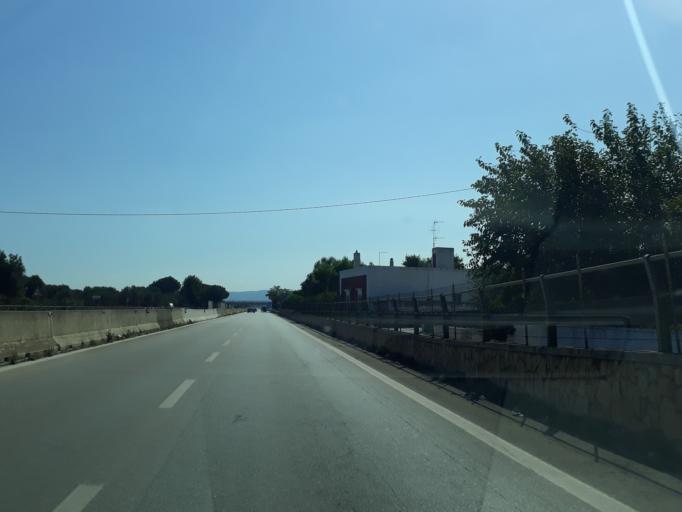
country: IT
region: Apulia
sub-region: Provincia di Brindisi
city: Fasano
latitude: 40.8788
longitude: 17.3390
